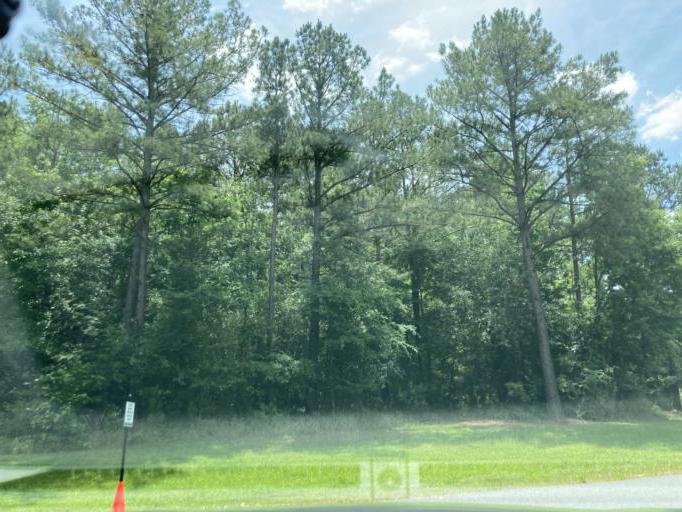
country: US
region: Georgia
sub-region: Bibb County
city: Macon
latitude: 32.8762
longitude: -83.6548
